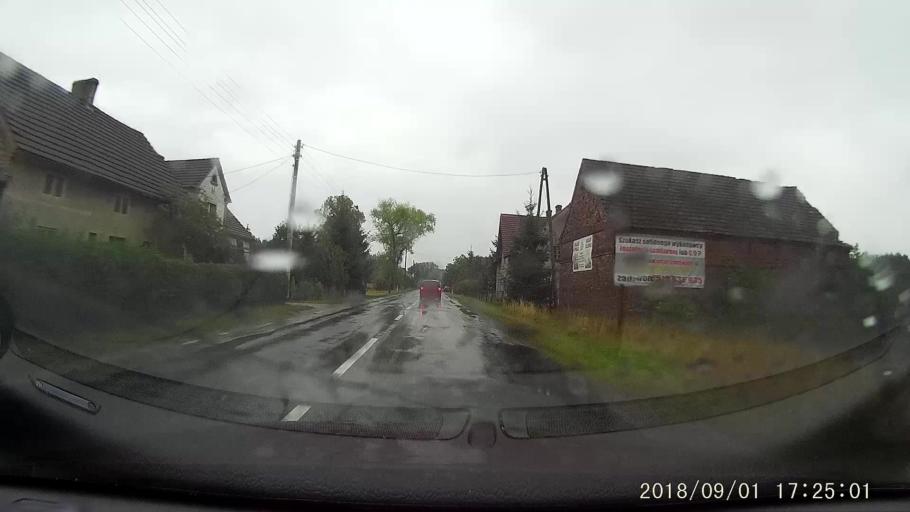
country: PL
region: Lubusz
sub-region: Powiat zaganski
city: Zagan
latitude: 51.6893
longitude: 15.3061
